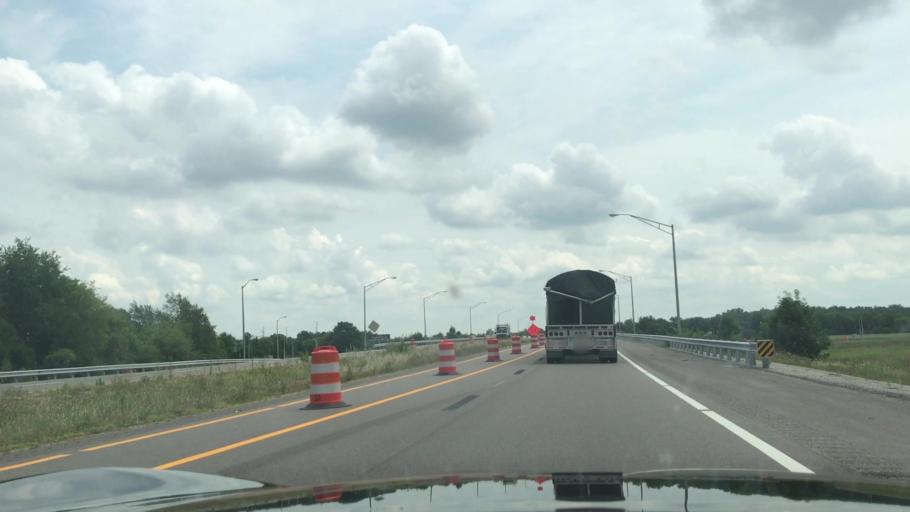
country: US
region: Kentucky
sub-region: Warren County
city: Bowling Green
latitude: 36.9602
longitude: -86.4977
